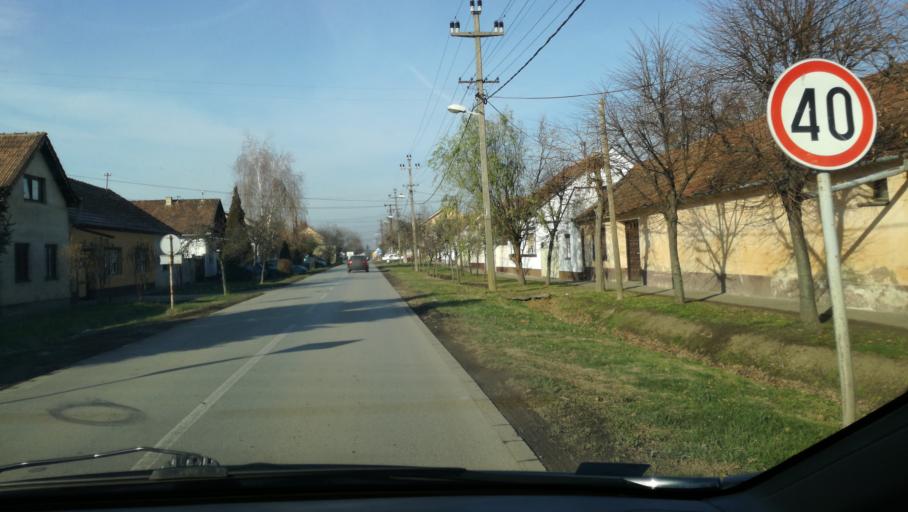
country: RS
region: Autonomna Pokrajina Vojvodina
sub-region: Severnobanatski Okrug
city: Kikinda
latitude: 45.8154
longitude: 20.4537
